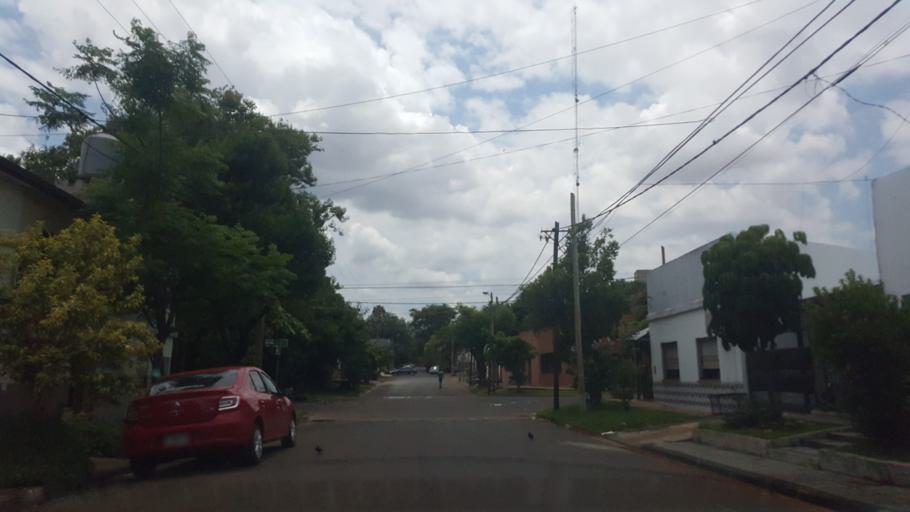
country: AR
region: Misiones
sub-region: Departamento de Capital
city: Posadas
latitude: -27.3837
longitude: -55.8973
